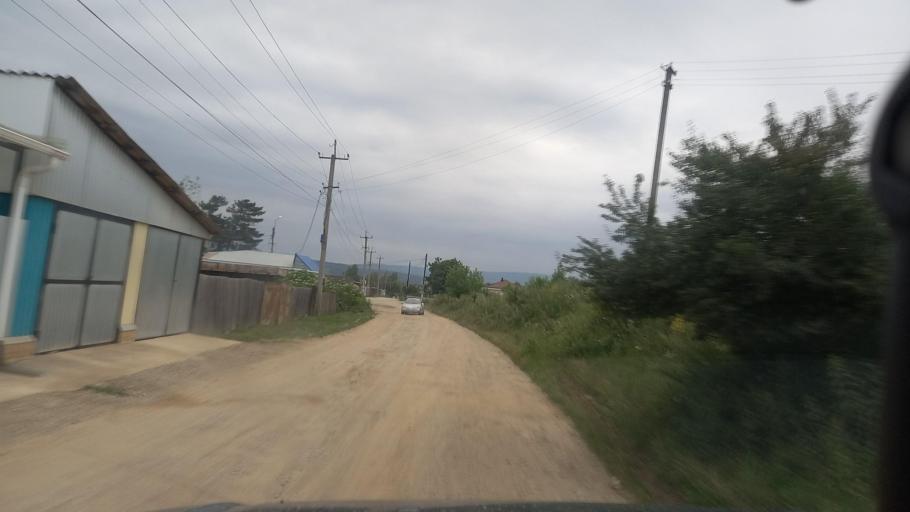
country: RU
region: Karachayevo-Cherkesiya
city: Pregradnaya
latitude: 43.9483
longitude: 41.1857
